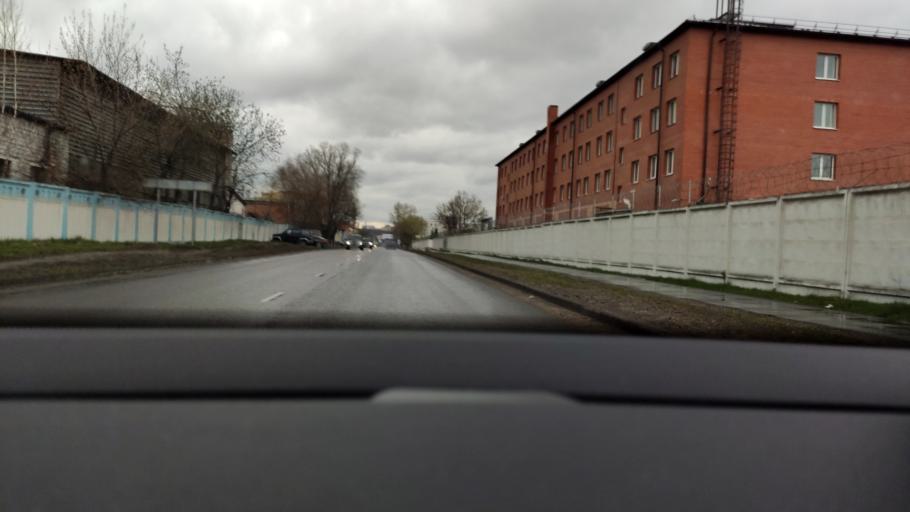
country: RU
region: Moskovskaya
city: Reutov
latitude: 55.7751
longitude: 37.8678
